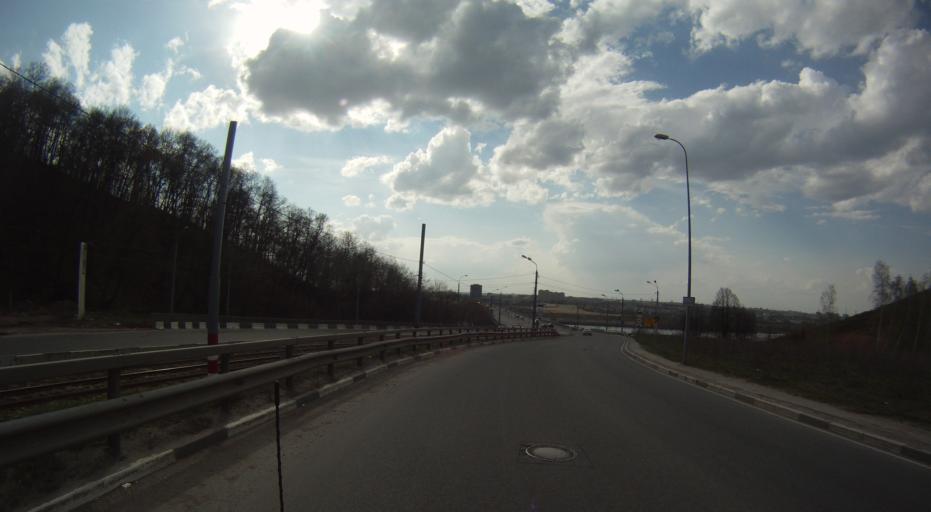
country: RU
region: Nizjnij Novgorod
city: Nizhniy Novgorod
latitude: 56.2986
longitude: 43.9717
